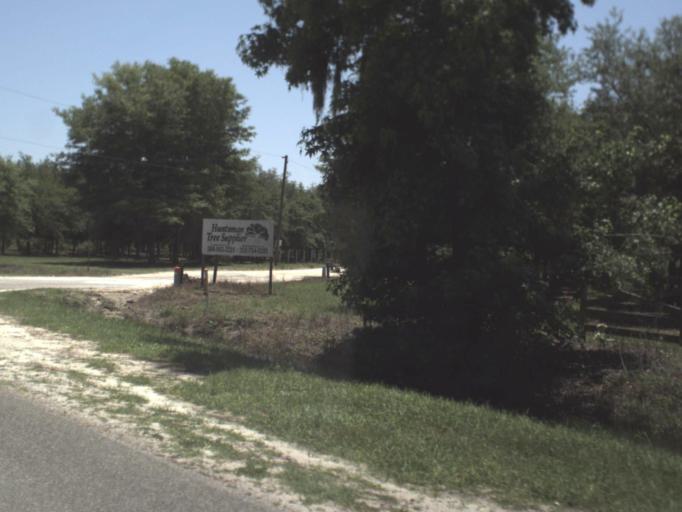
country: US
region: Florida
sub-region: Suwannee County
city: Wellborn
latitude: 30.2072
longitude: -82.8076
